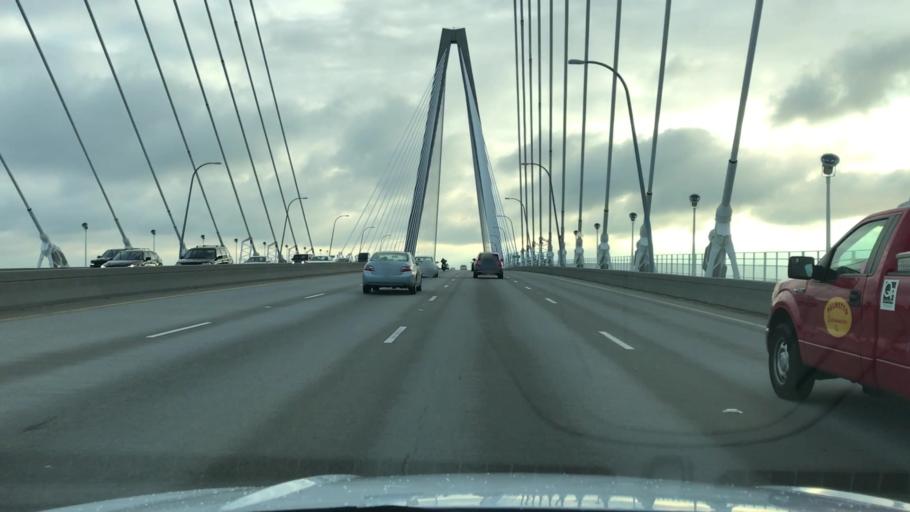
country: US
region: South Carolina
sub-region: Charleston County
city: Charleston
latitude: 32.8031
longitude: -79.9167
